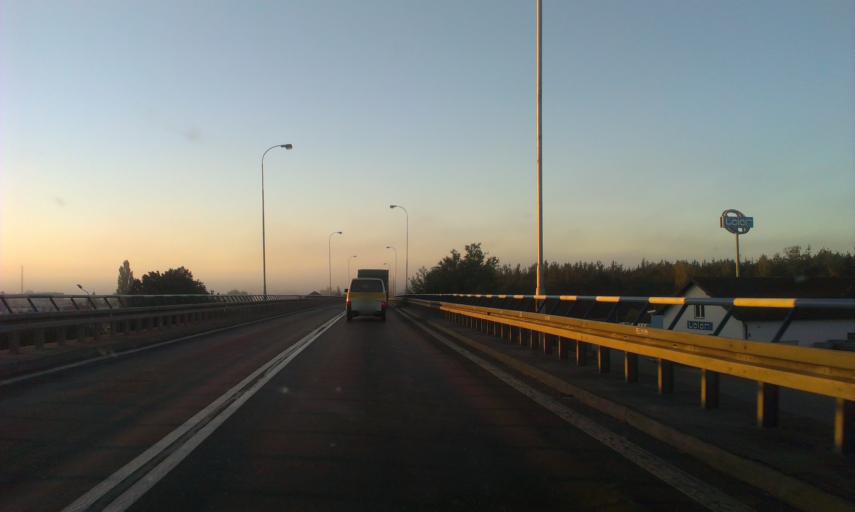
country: PL
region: Kujawsko-Pomorskie
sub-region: Powiat swiecki
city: Swiecie
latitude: 53.3999
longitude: 18.3998
